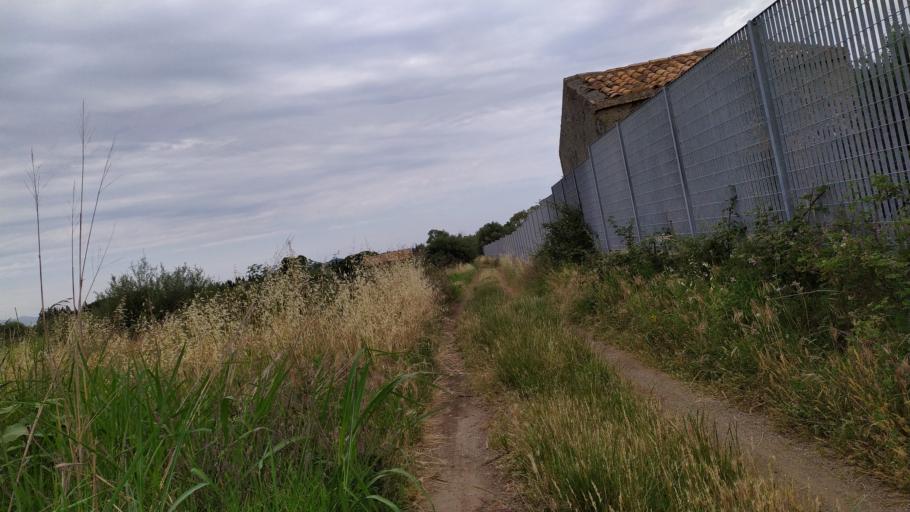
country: IT
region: Sicily
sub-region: Messina
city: San Filippo del Mela
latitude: 38.1836
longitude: 15.2641
